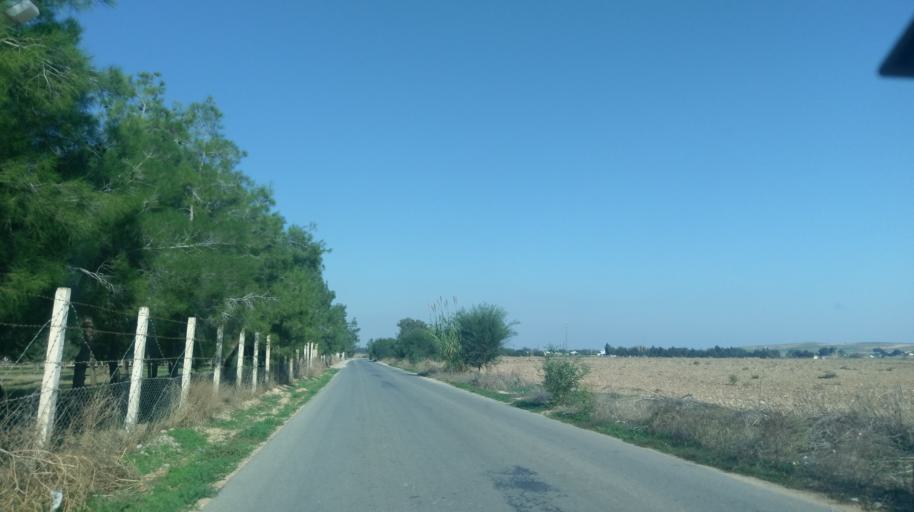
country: CY
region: Larnaka
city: Troulloi
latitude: 35.0843
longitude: 33.6140
